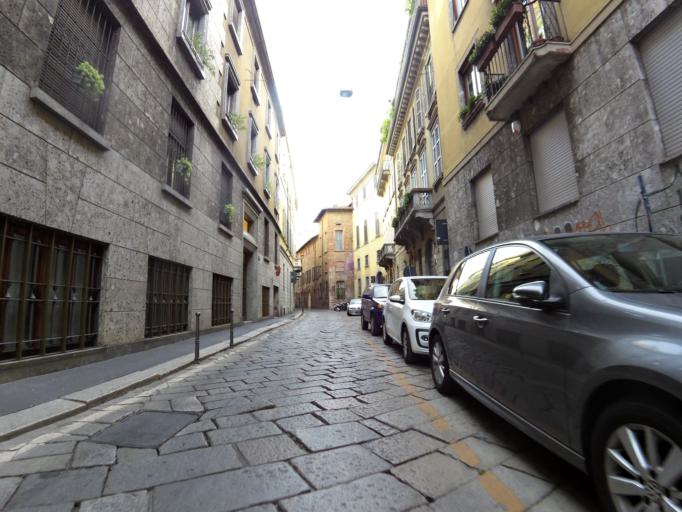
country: IT
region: Lombardy
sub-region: Citta metropolitana di Milano
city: Milano
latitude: 45.4634
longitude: 9.1794
